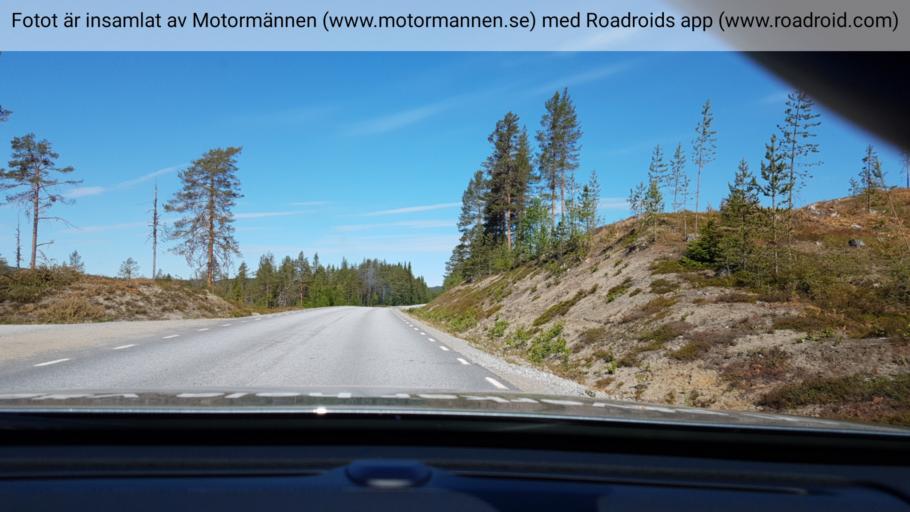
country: SE
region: Vaesterbotten
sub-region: Bjurholms Kommun
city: Bjurholm
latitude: 64.0116
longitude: 18.7046
